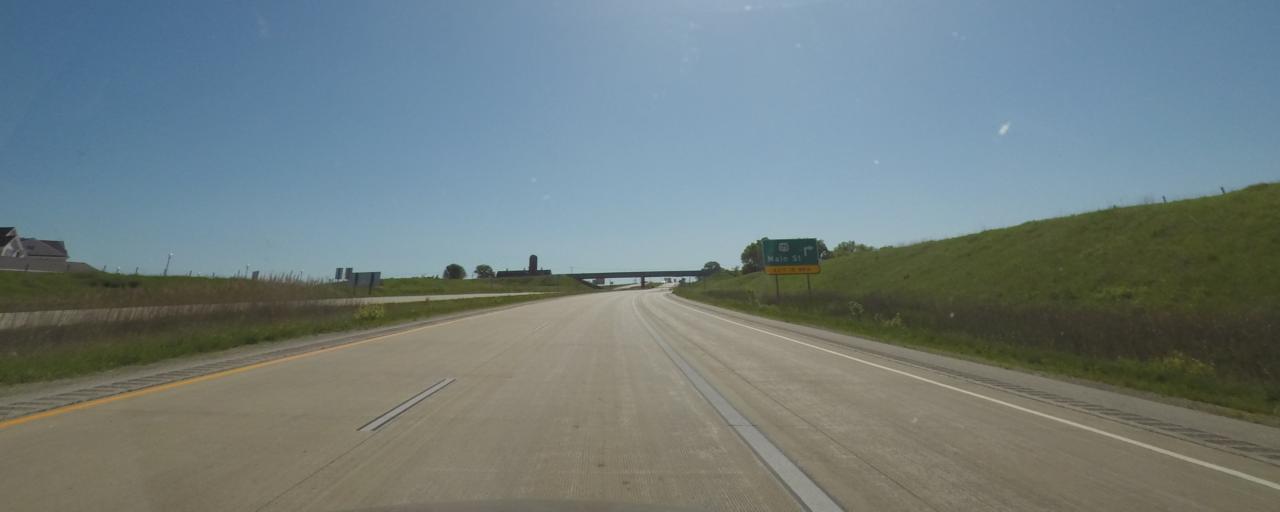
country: US
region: Wisconsin
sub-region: Fond du Lac County
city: Fond du Lac
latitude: 43.7372
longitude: -88.4546
